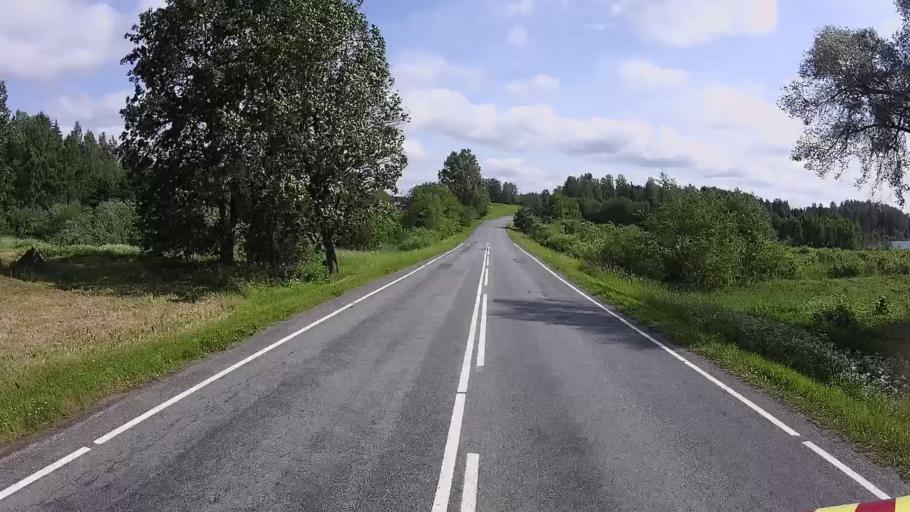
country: EE
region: Vorumaa
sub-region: Antsla vald
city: Vana-Antsla
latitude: 57.8738
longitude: 26.6263
